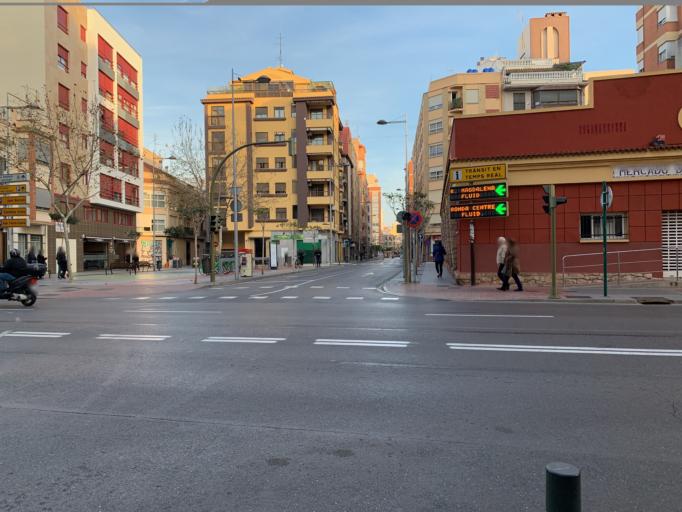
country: ES
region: Valencia
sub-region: Provincia de Castello
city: Castello de la Plana
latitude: 39.9898
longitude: -0.0407
